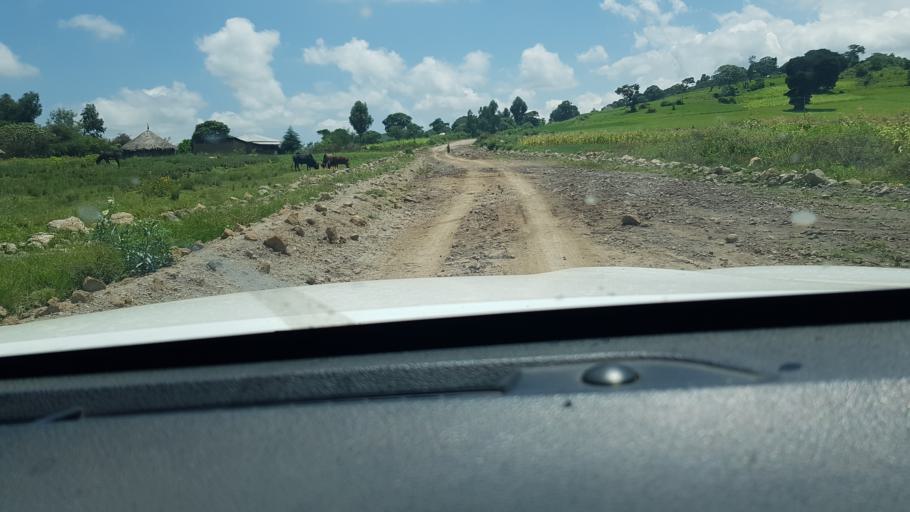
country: ET
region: Oromiya
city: Sirre
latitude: 8.4396
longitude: 39.8807
